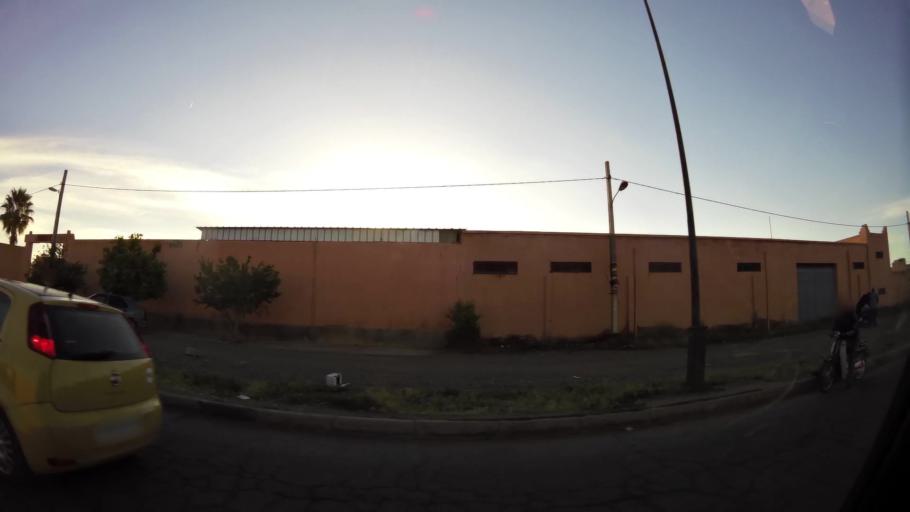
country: MA
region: Marrakech-Tensift-Al Haouz
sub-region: Marrakech
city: Marrakesh
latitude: 31.6239
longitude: -8.0435
